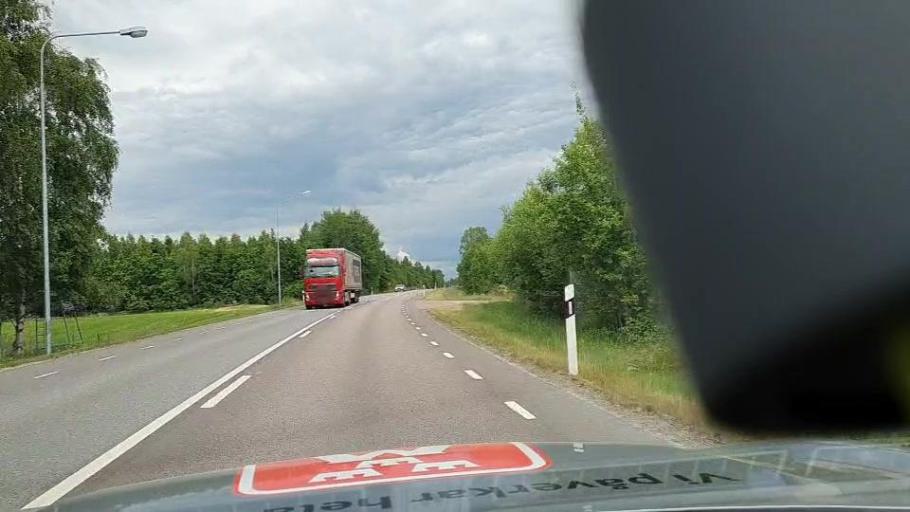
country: SE
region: Blekinge
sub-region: Karlskrona Kommun
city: Rodeby
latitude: 56.4337
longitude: 15.5398
